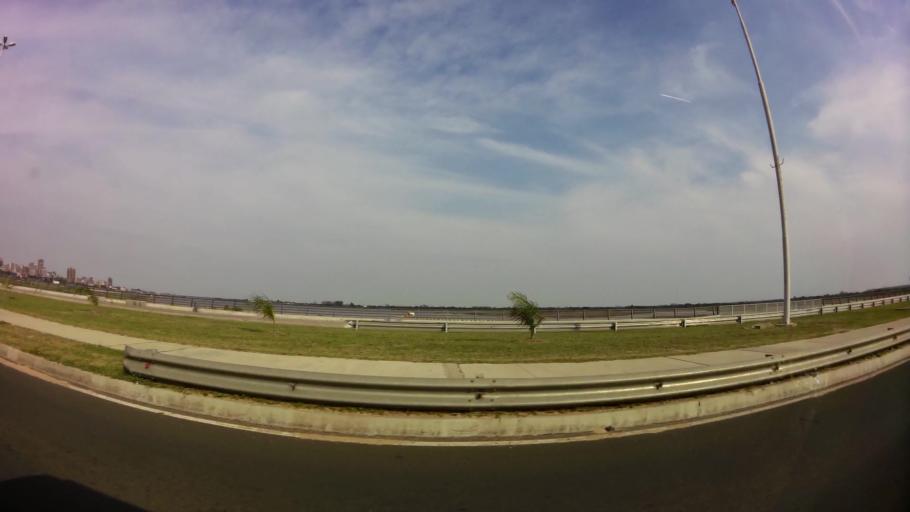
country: PY
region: Asuncion
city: Asuncion
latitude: -25.2737
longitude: -57.6164
